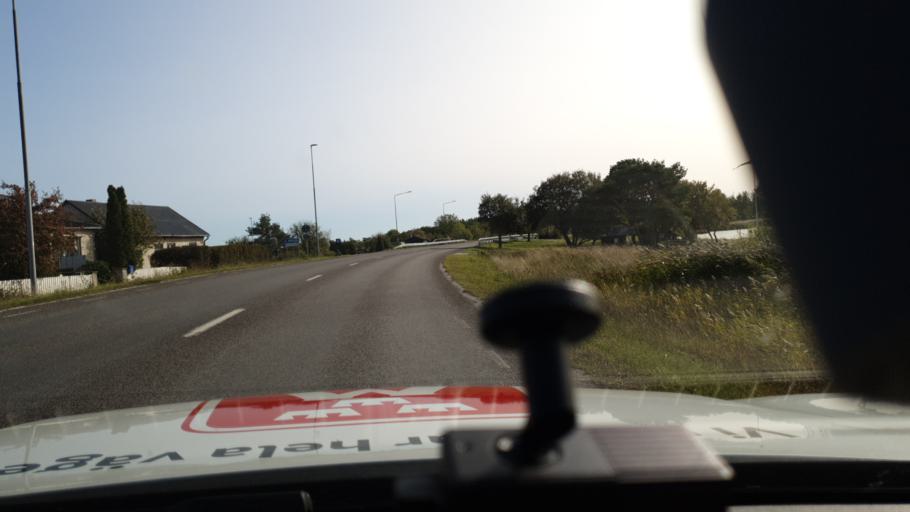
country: SE
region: Gotland
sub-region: Gotland
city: Slite
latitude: 57.6962
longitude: 18.7981
